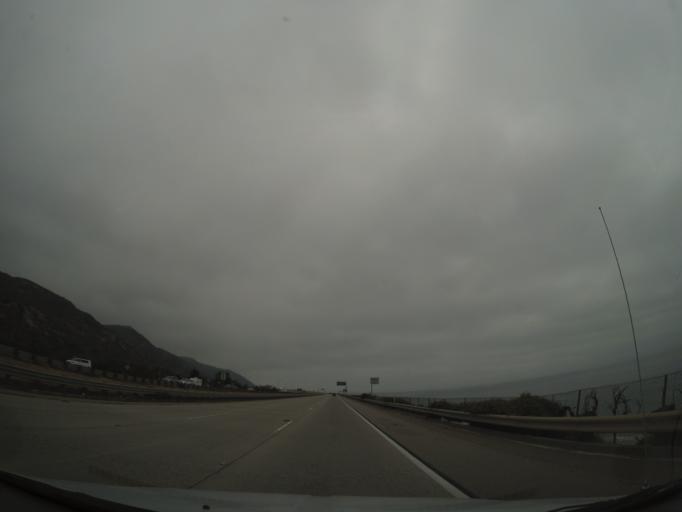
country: US
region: California
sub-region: Santa Barbara County
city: Carpinteria
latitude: 34.3494
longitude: -119.4245
